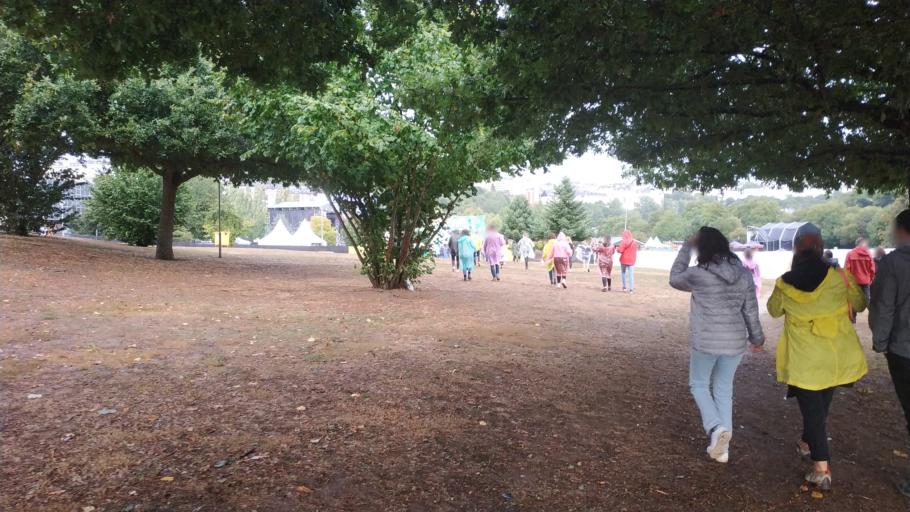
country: ES
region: Galicia
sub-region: Provincia de Lugo
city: Lugo
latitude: 43.0022
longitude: -7.5691
